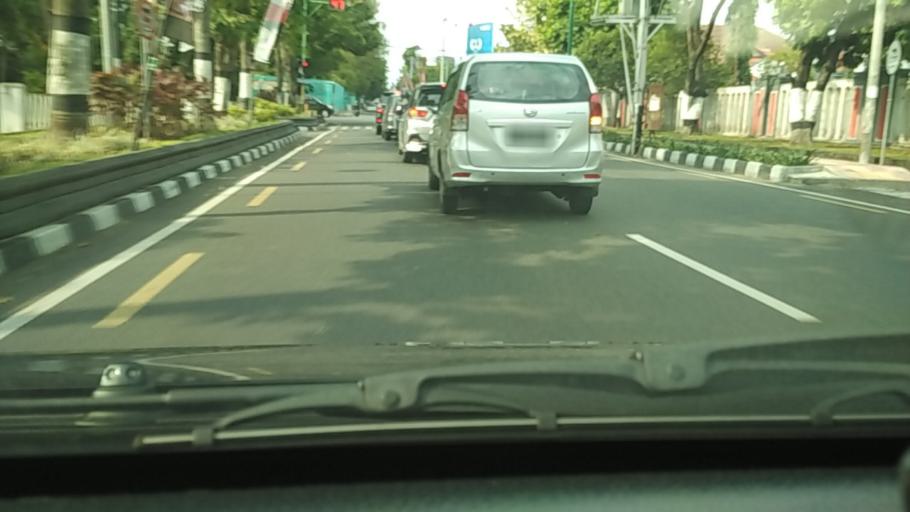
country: ID
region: Daerah Istimewa Yogyakarta
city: Yogyakarta
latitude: -7.7982
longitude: 110.3848
